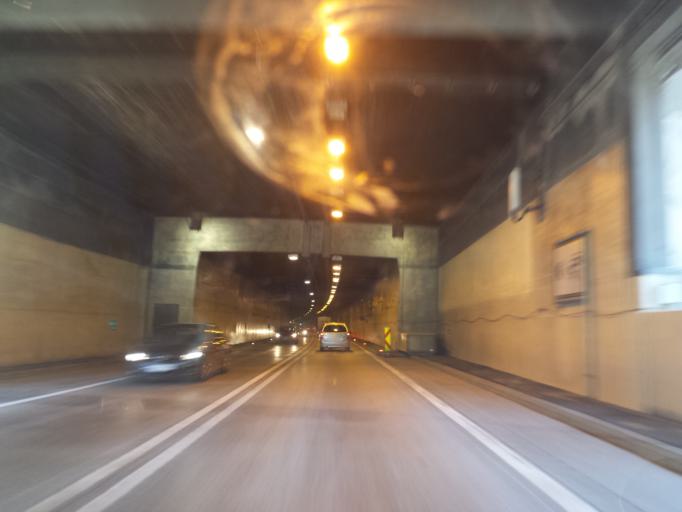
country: AT
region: Styria
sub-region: Politischer Bezirk Graz-Umgebung
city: Ubelbach
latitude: 47.2486
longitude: 15.1588
